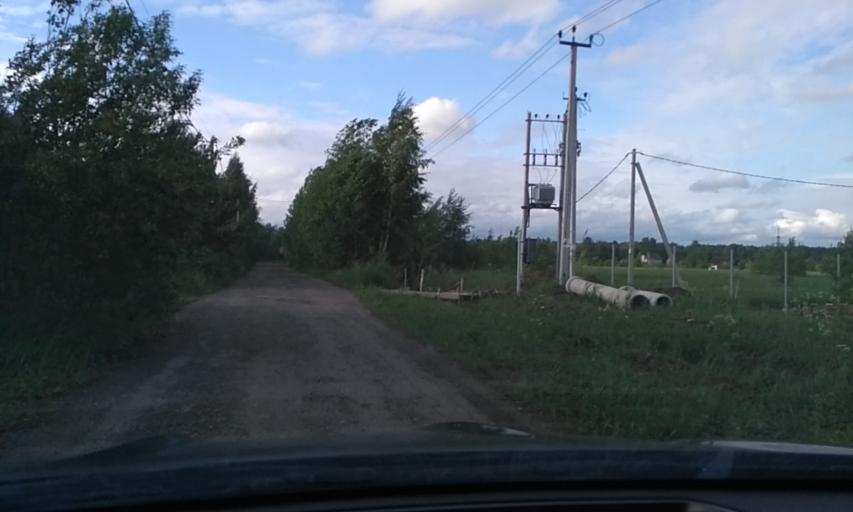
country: RU
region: Leningrad
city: Otradnoye
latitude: 59.8087
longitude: 30.8270
